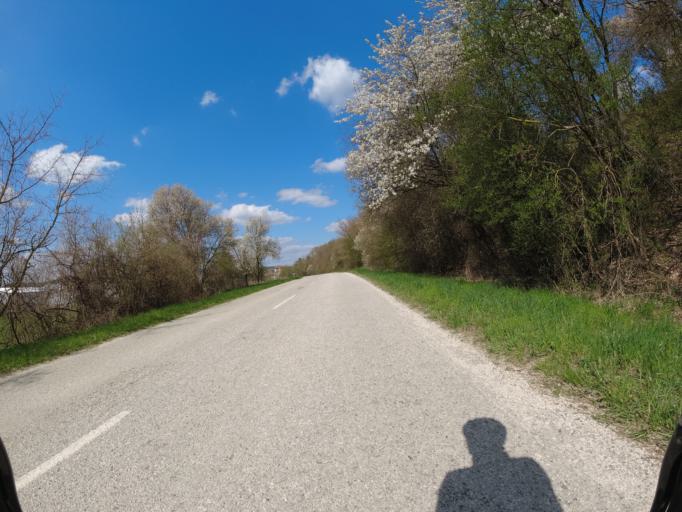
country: SK
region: Nitriansky
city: Stara Tura
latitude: 48.7293
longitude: 17.7233
